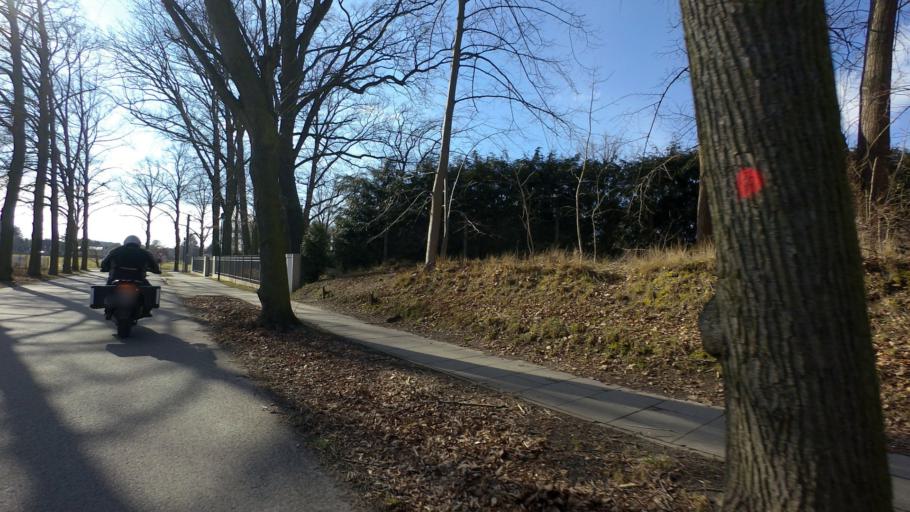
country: DE
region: Brandenburg
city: Wandlitz
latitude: 52.7503
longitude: 13.4570
